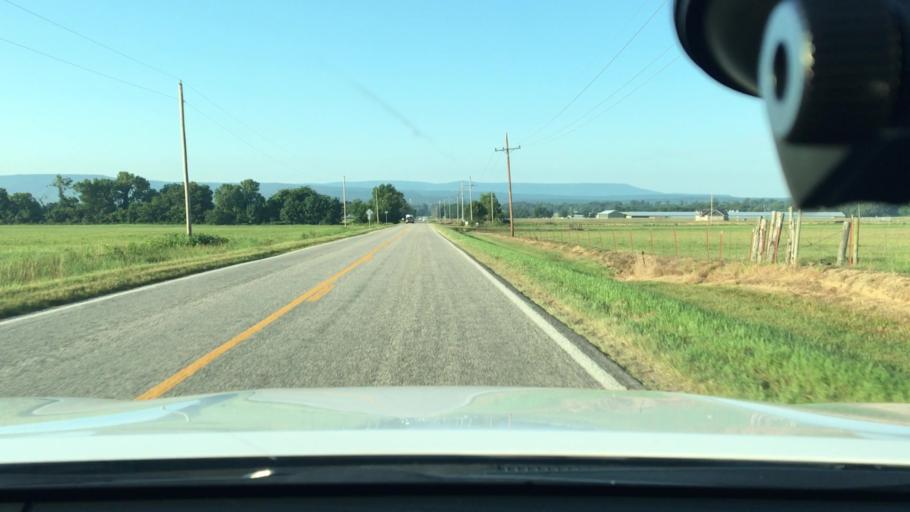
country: US
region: Arkansas
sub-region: Logan County
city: Paris
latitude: 35.3358
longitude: -93.6319
